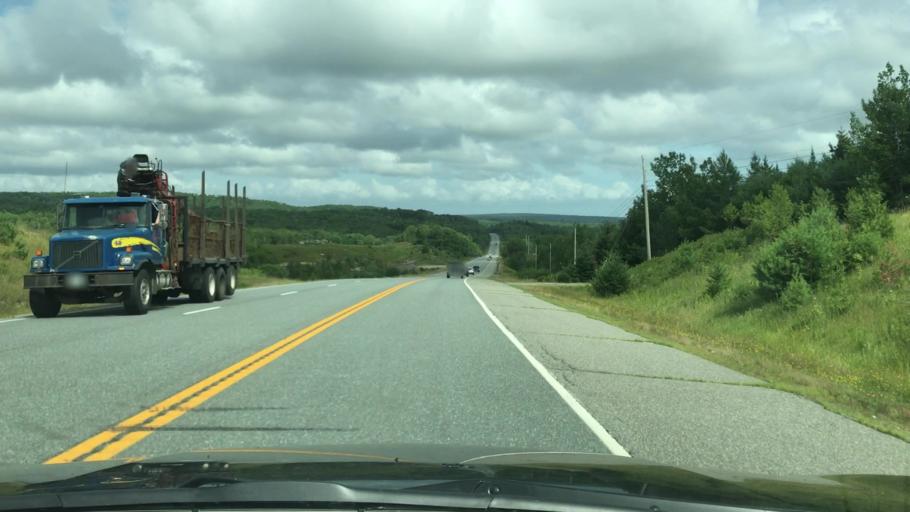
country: US
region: Maine
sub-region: Hancock County
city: Orland
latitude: 44.5677
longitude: -68.6229
